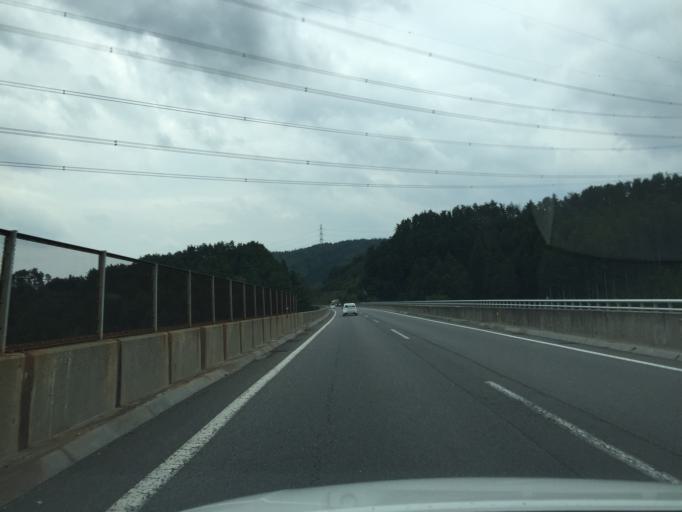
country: JP
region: Fukushima
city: Iwaki
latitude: 37.1591
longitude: 140.7325
